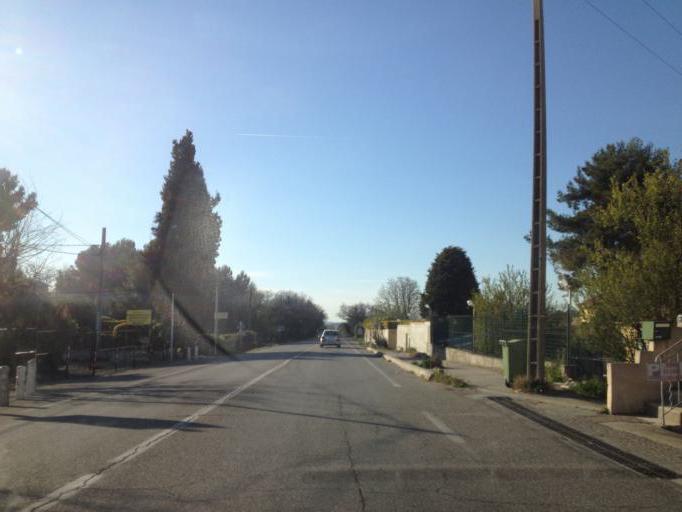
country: FR
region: Provence-Alpes-Cote d'Azur
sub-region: Departement des Bouches-du-Rhone
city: Aix-en-Provence
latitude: 43.5567
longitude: 5.4183
